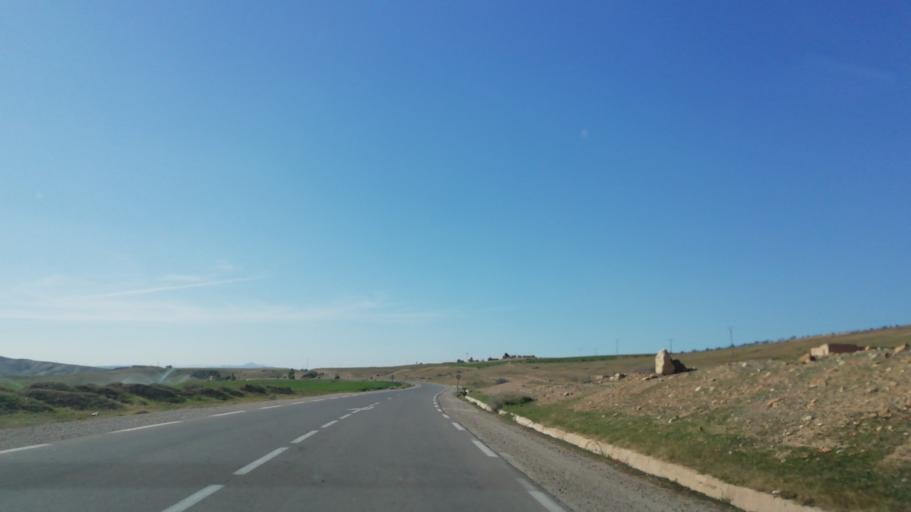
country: DZ
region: Mascara
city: Oued el Abtal
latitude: 35.4519
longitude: 0.7786
